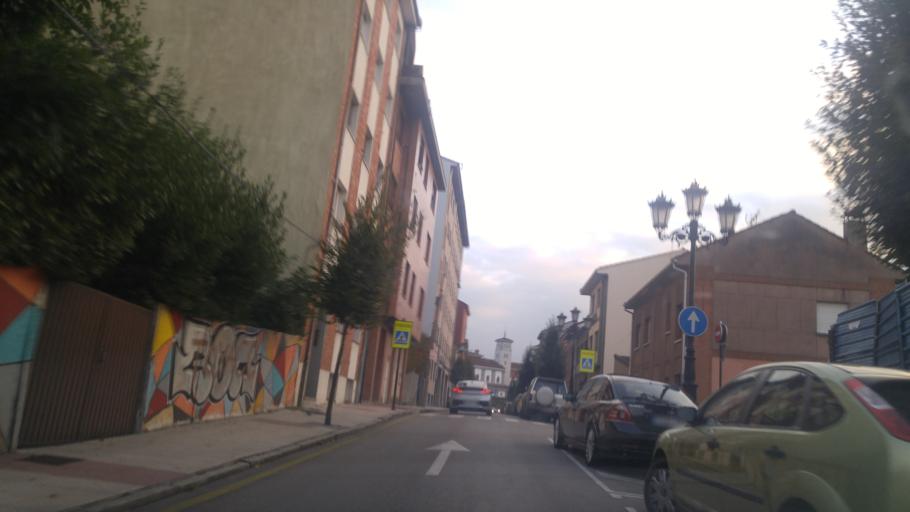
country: ES
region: Asturias
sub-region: Province of Asturias
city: Oviedo
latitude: 43.3721
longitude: -5.8571
